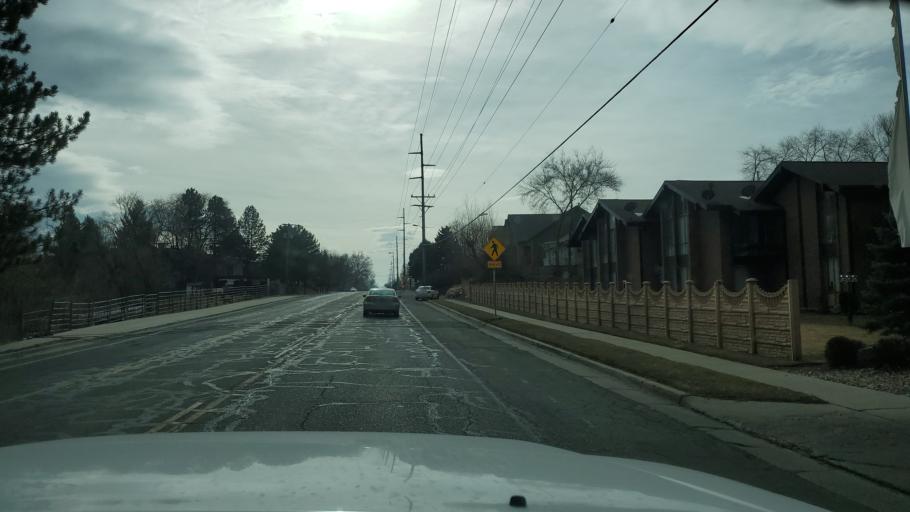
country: US
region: Utah
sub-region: Salt Lake County
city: Millcreek
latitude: 40.6833
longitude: -111.8656
